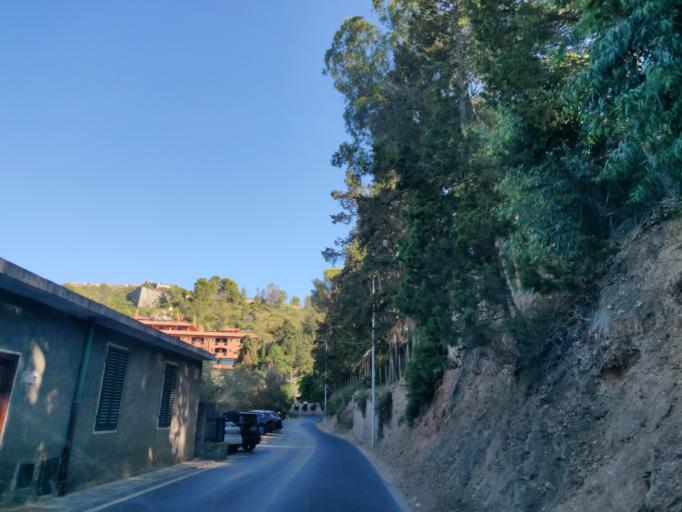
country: IT
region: Tuscany
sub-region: Provincia di Grosseto
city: Porto Ercole
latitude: 42.3907
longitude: 11.2071
